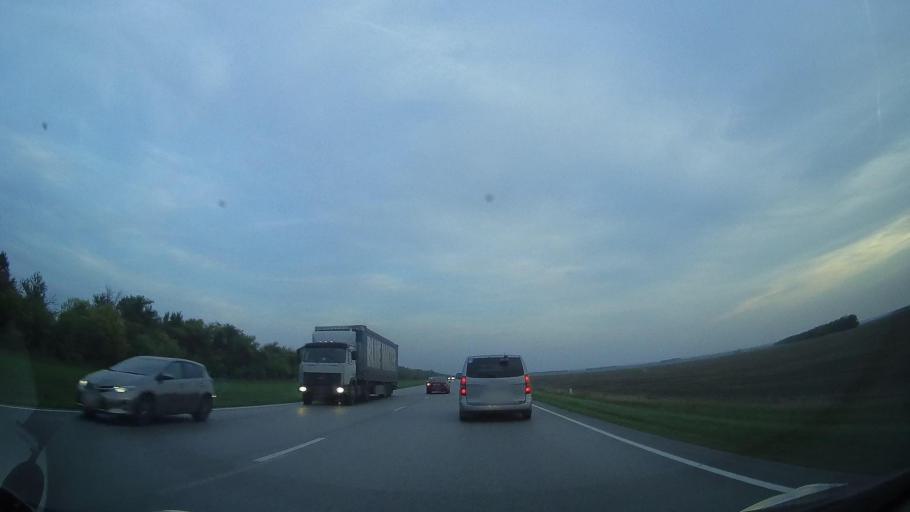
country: RU
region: Rostov
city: Kagal'nitskaya
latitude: 46.9214
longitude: 40.1046
